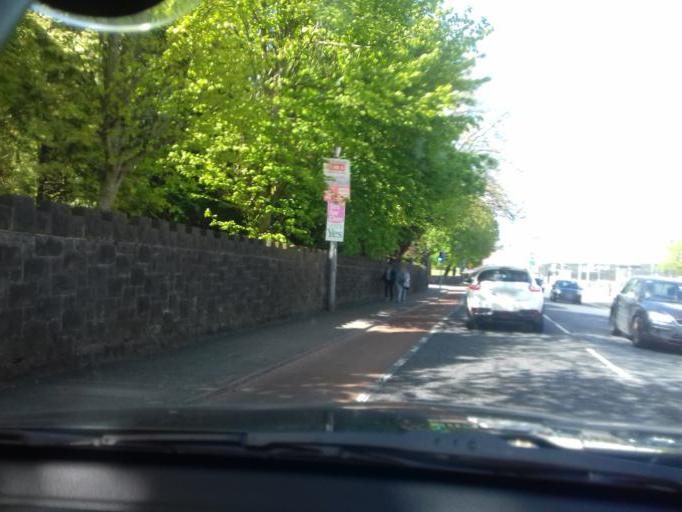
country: IE
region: Munster
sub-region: Waterford
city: Waterford
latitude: 52.2552
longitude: -7.1020
